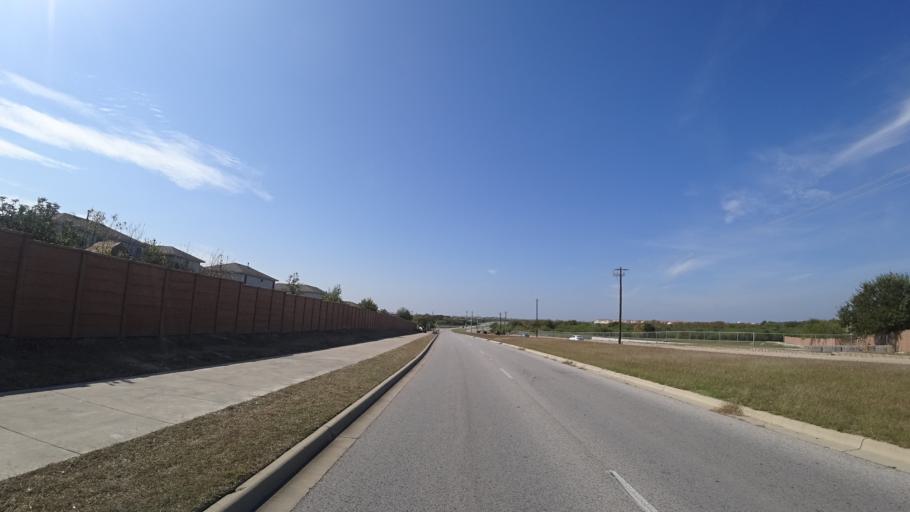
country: US
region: Texas
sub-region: Travis County
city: Pflugerville
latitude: 30.4293
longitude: -97.6396
